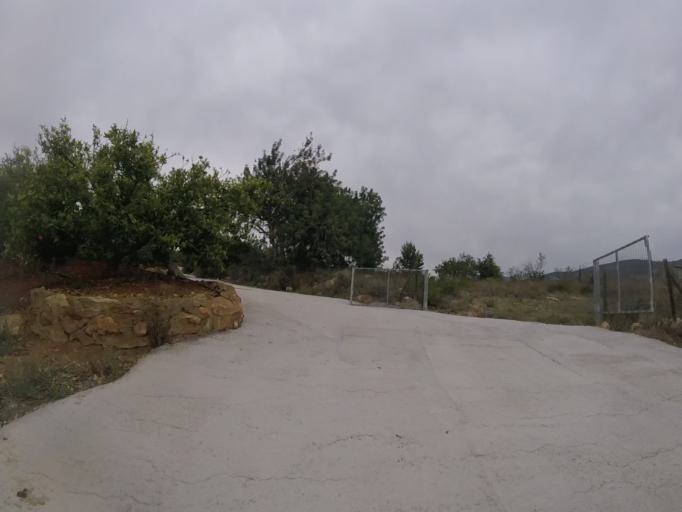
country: ES
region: Valencia
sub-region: Provincia de Castello
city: Alcala de Xivert
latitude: 40.2772
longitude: 0.2534
